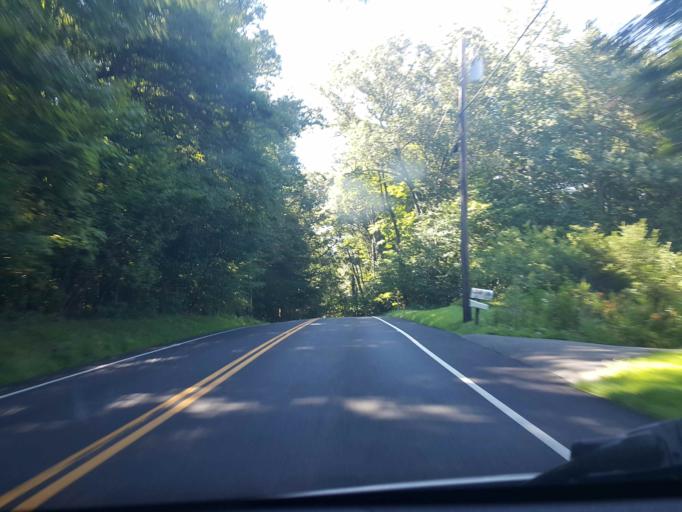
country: US
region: Connecticut
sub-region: New Haven County
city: North Branford
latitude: 41.3483
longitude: -72.7167
